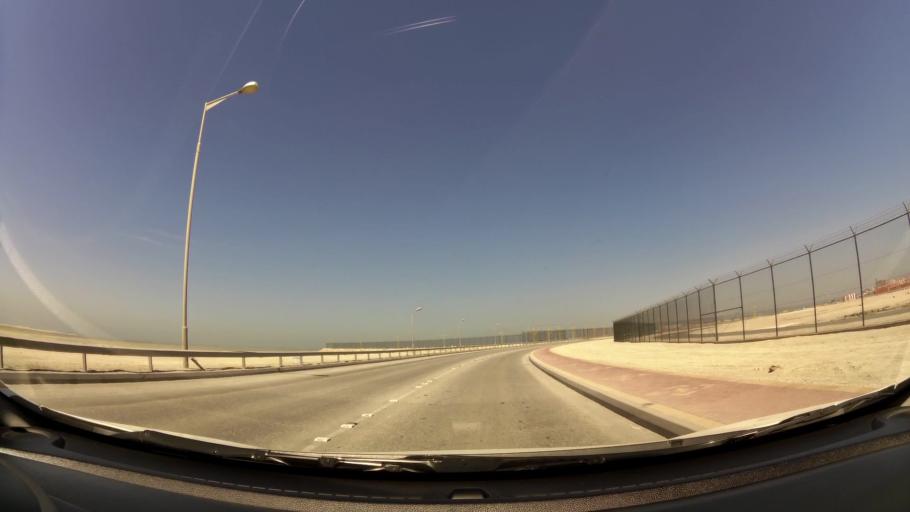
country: BH
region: Muharraq
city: Al Muharraq
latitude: 26.2815
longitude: 50.6131
